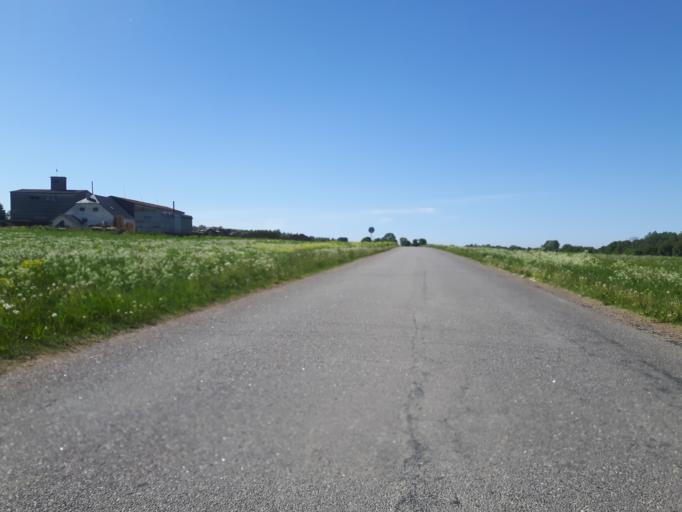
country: EE
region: Laeaene-Virumaa
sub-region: Haljala vald
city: Haljala
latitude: 59.5388
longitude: 26.2321
